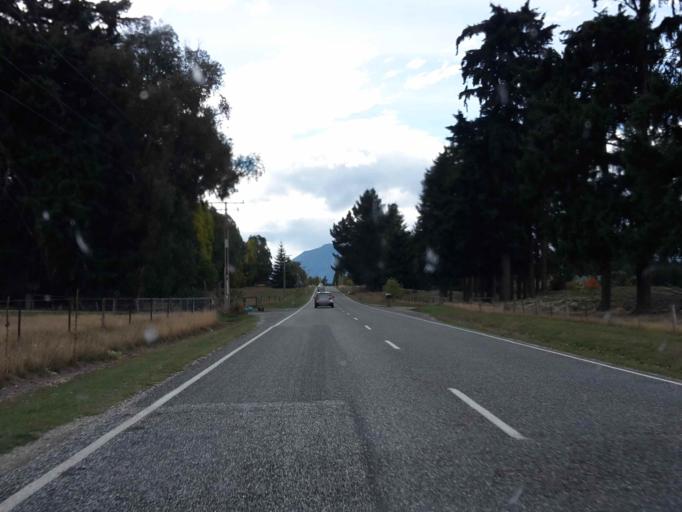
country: NZ
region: Otago
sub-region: Queenstown-Lakes District
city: Wanaka
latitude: -44.7217
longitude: 169.1369
